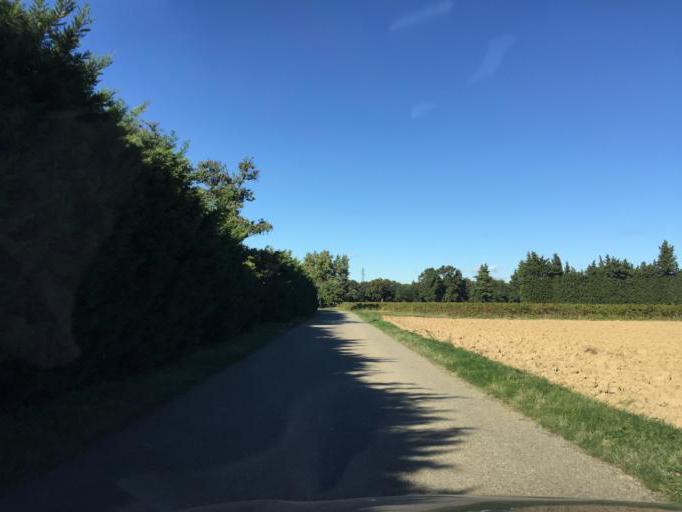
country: FR
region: Provence-Alpes-Cote d'Azur
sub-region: Departement du Vaucluse
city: Piolenc
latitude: 44.1680
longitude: 4.7896
